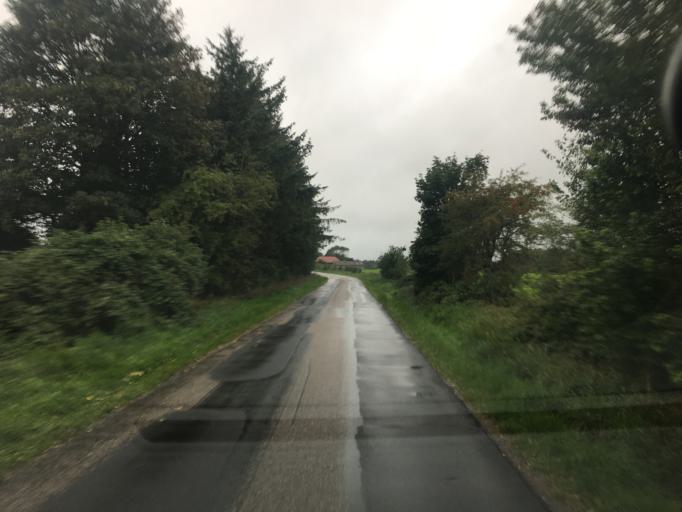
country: DE
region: Schleswig-Holstein
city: Bramstedtlund
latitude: 54.9577
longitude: 9.0438
